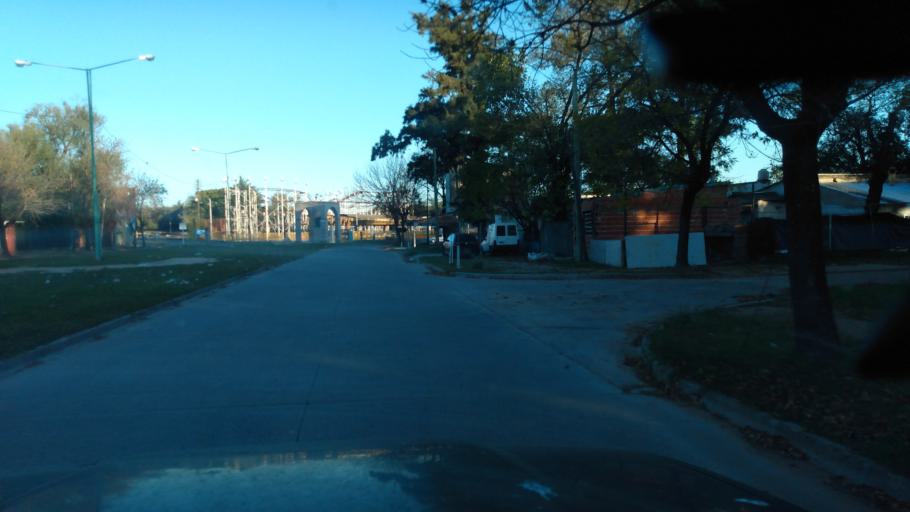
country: AR
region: Buenos Aires
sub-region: Partido de Lujan
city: Lujan
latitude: -34.5637
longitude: -59.1258
